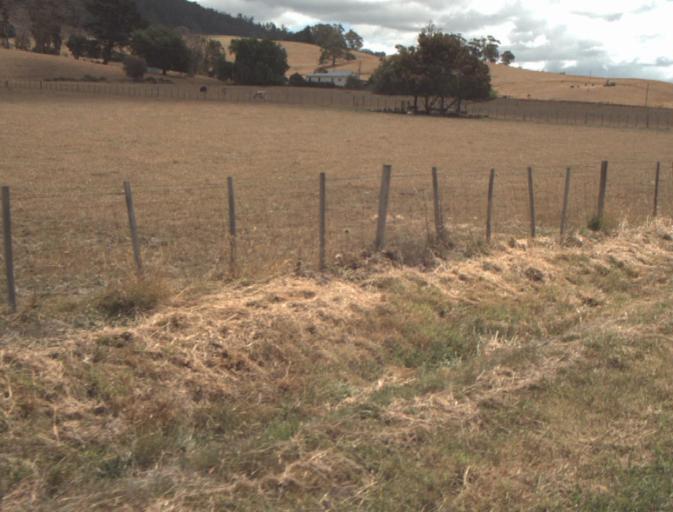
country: AU
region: Tasmania
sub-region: Launceston
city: Mayfield
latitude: -41.2310
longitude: 147.1246
